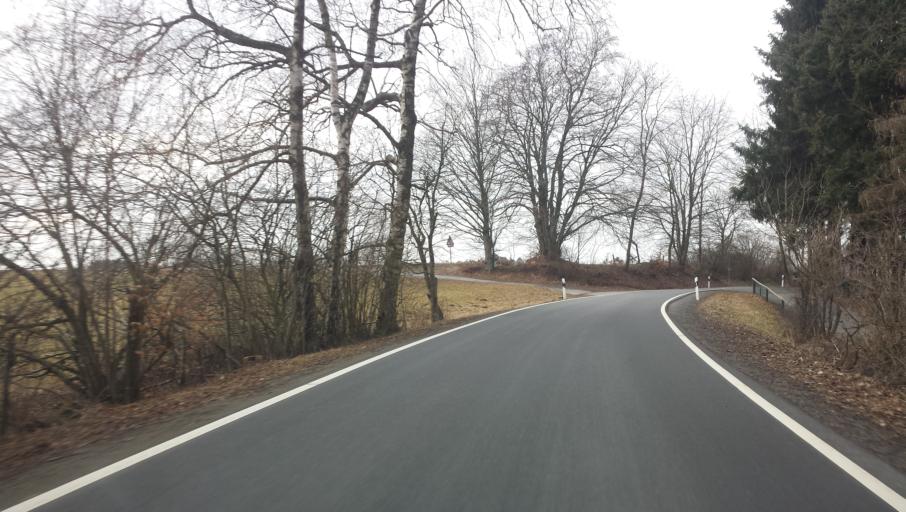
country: DE
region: Hesse
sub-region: Regierungsbezirk Darmstadt
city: Lindenfels
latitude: 49.6909
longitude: 8.7289
